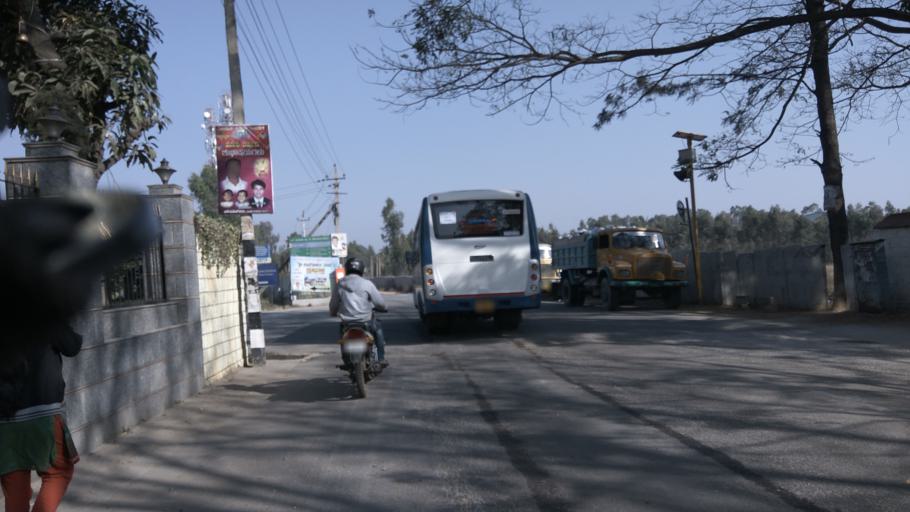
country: IN
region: Karnataka
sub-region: Bangalore Rural
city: Devanhalli
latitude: 13.1930
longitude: 77.6458
